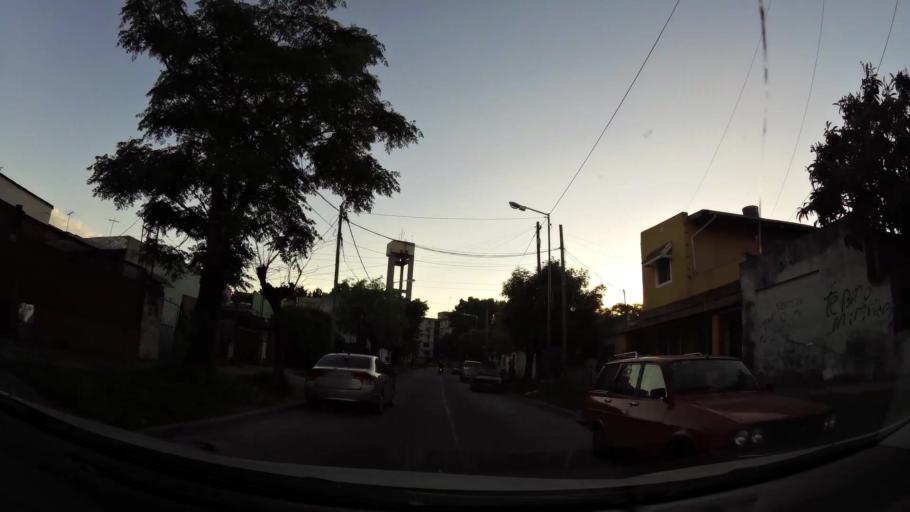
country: AR
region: Buenos Aires
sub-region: Partido de Tigre
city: Tigre
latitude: -34.4456
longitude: -58.5734
